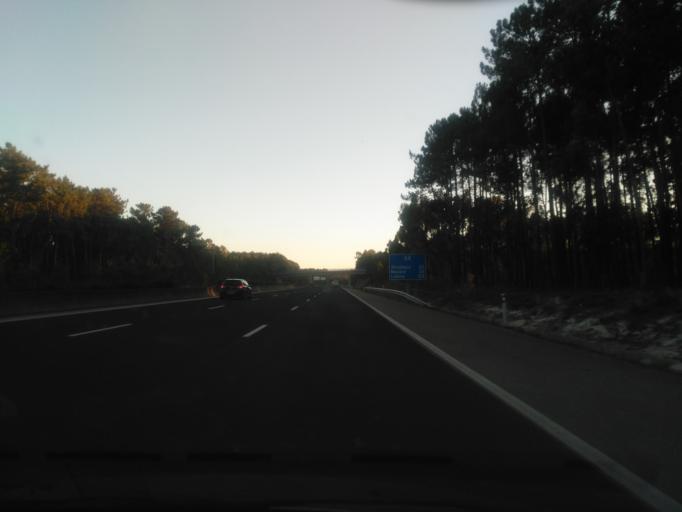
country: PT
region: Leiria
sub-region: Leiria
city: Maceira
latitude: 39.7059
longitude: -8.9197
